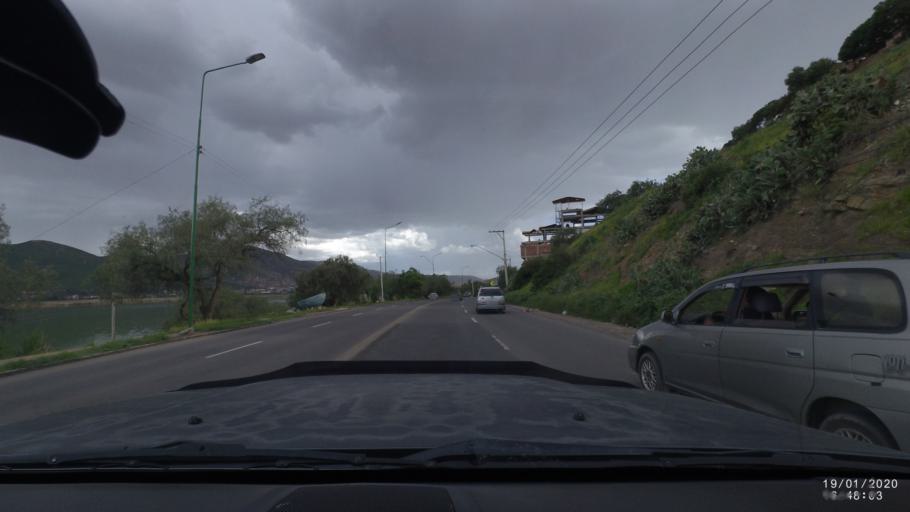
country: BO
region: Cochabamba
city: Cochabamba
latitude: -17.4081
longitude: -66.1435
